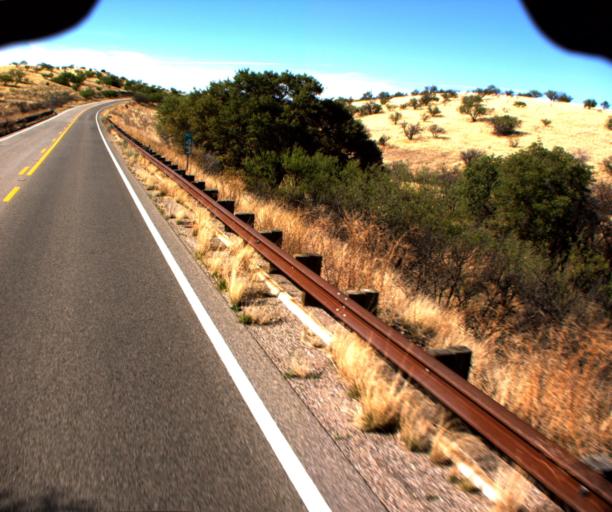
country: US
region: Arizona
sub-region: Pima County
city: Corona de Tucson
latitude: 31.8092
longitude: -110.7101
